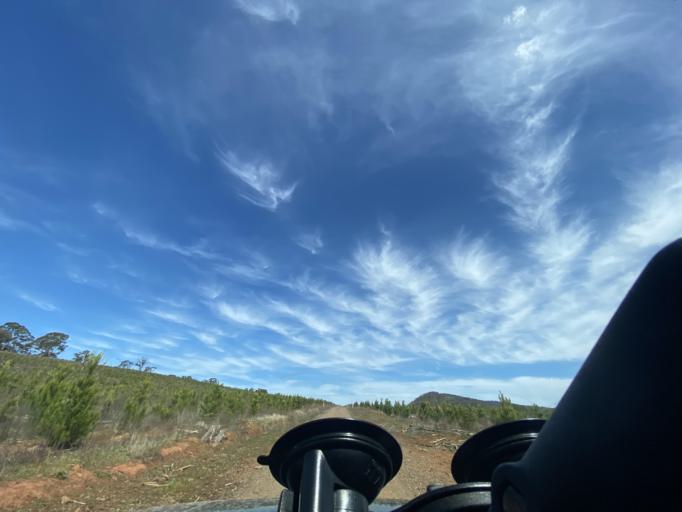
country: AU
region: Victoria
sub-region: Mansfield
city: Mansfield
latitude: -36.8205
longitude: 146.1026
